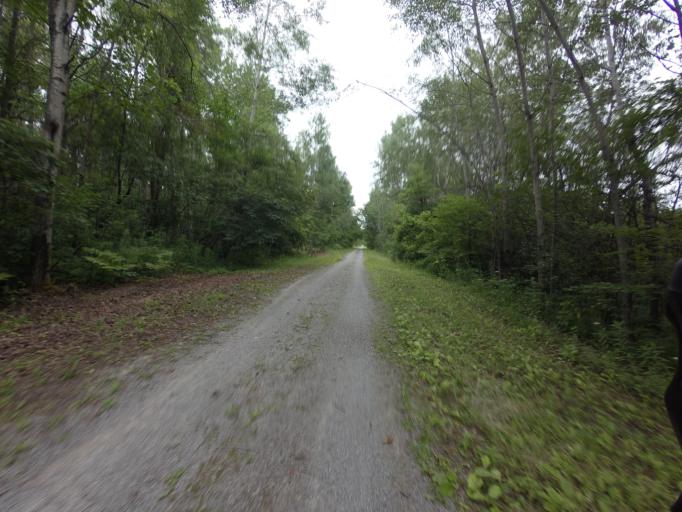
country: CA
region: Ontario
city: Ottawa
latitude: 45.2616
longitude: -75.6229
